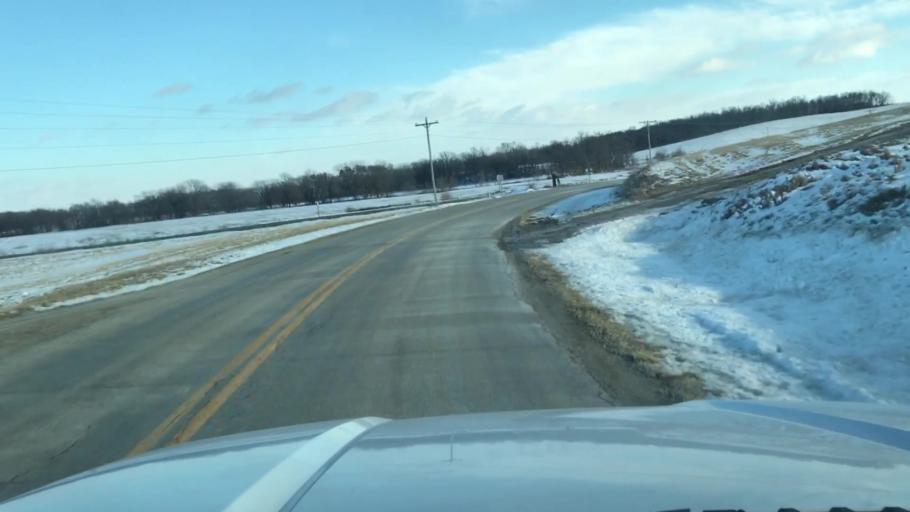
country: US
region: Missouri
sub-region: Holt County
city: Oregon
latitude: 40.1004
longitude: -94.9766
